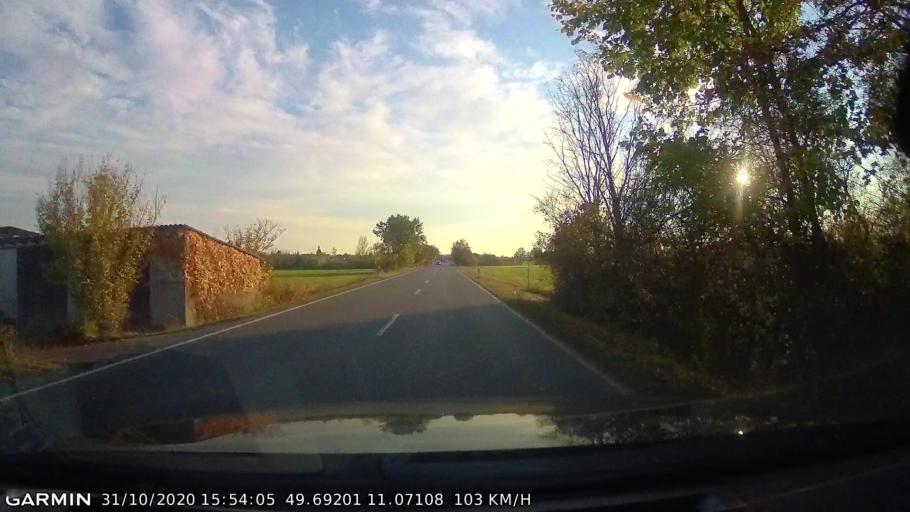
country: DE
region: Bavaria
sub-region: Upper Franconia
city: Poxdorf
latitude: 49.6918
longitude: 11.0709
